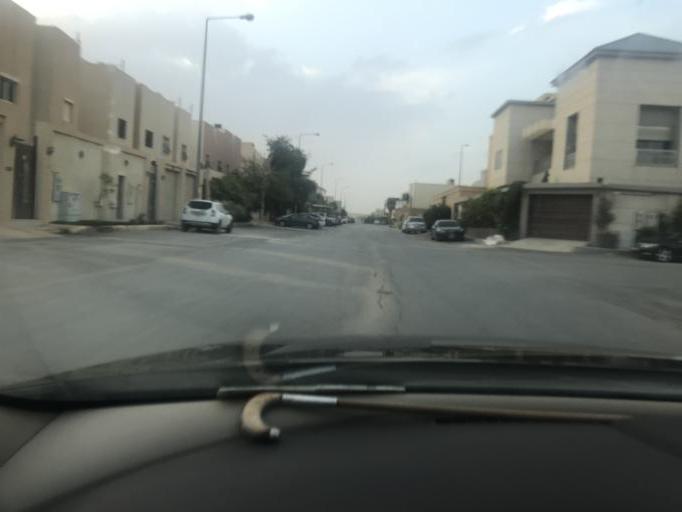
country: SA
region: Ar Riyad
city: Riyadh
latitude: 24.7277
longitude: 46.7456
